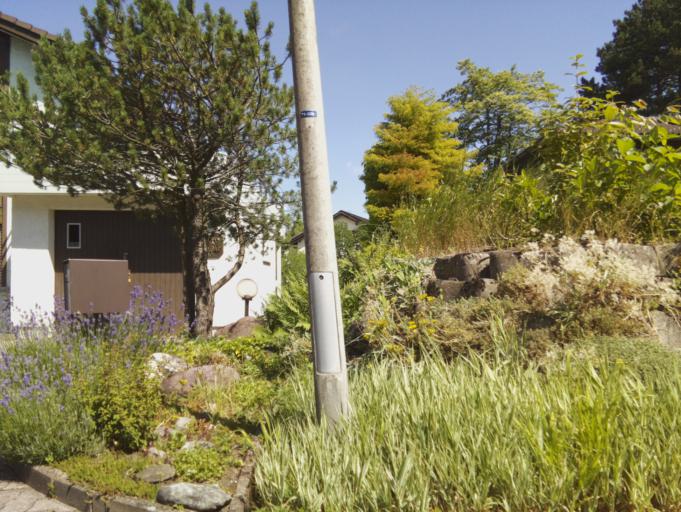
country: CH
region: Glarus
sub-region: Glarus
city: Niederurnen
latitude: 47.1236
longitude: 9.0583
